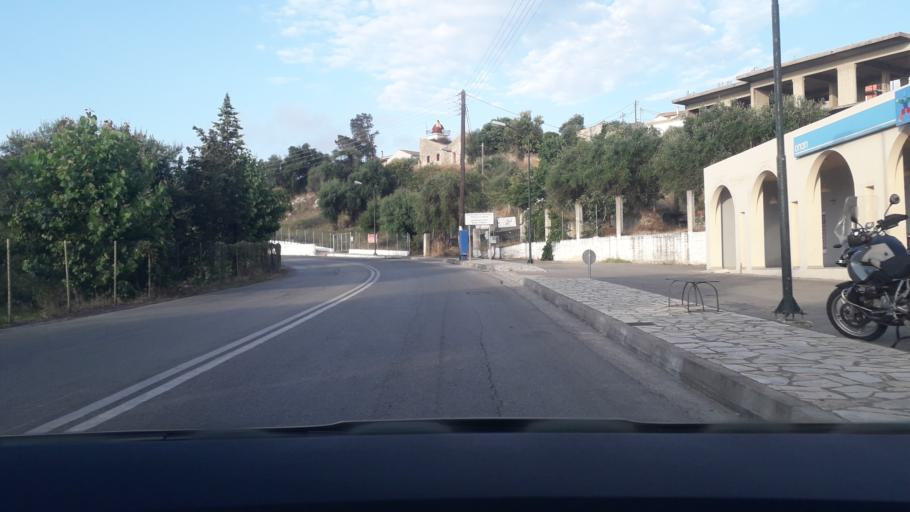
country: GR
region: Ionian Islands
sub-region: Nomos Kerkyras
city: Agios Matthaios
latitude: 39.4880
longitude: 19.9259
